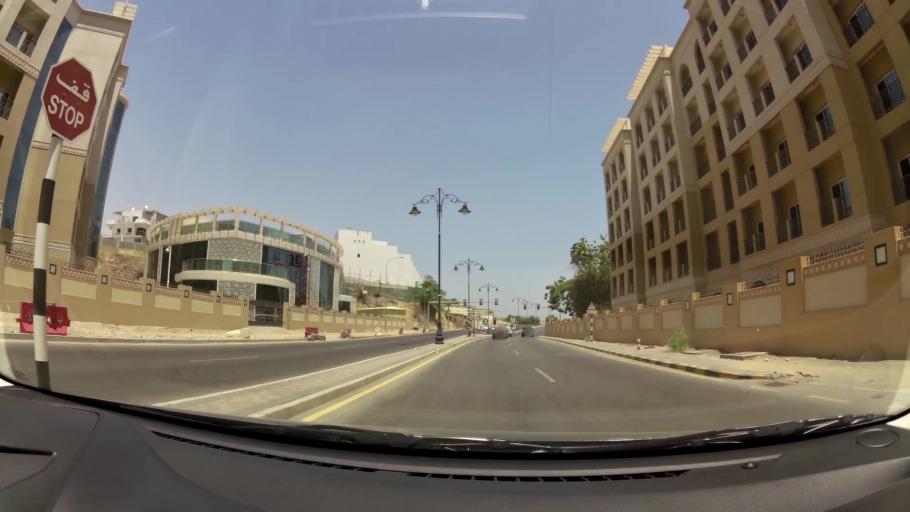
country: OM
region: Muhafazat Masqat
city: Bawshar
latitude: 23.6111
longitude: 58.4753
